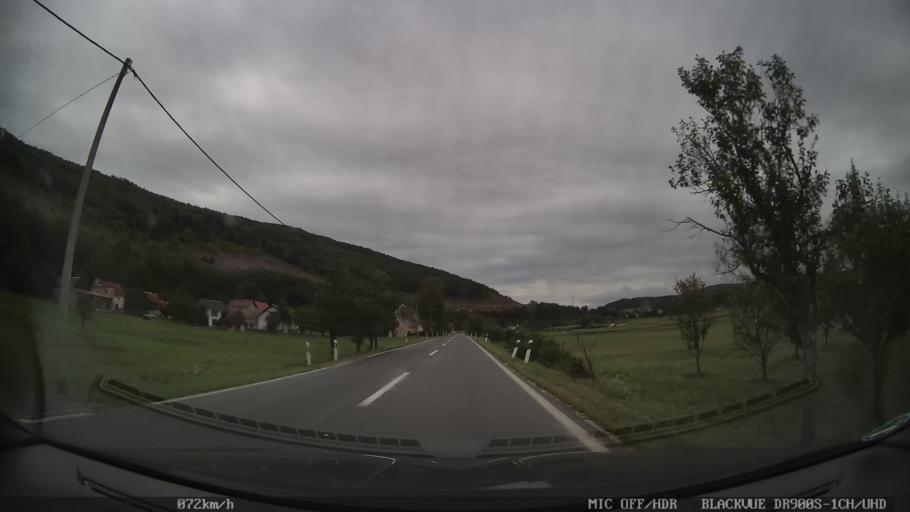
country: HR
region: Licko-Senjska
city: Otocac
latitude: 44.9023
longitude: 15.1774
